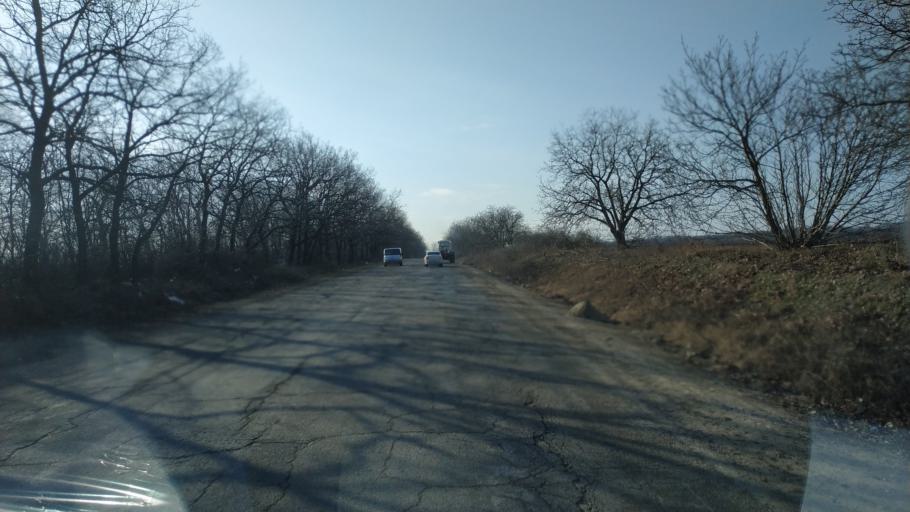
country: MD
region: Chisinau
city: Singera
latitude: 46.8715
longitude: 29.0397
